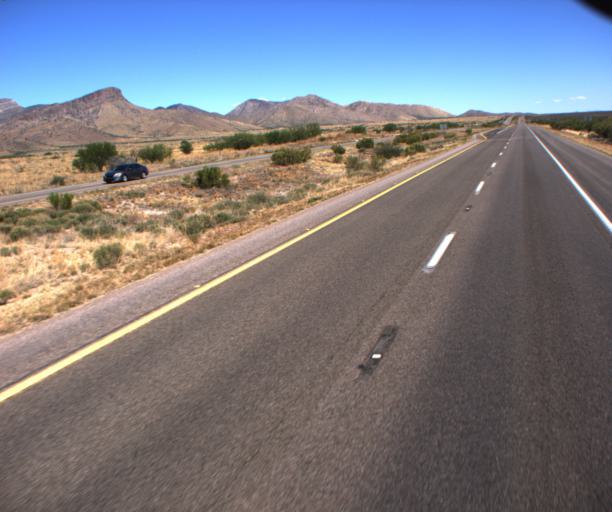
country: US
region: Arizona
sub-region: Cochise County
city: Huachuca City
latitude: 31.7793
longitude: -110.3500
